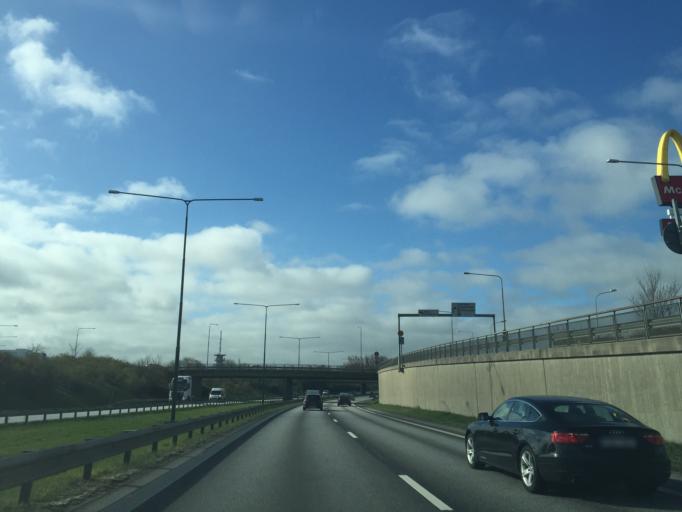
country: SE
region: Skane
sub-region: Burlovs Kommun
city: Arloev
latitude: 55.5841
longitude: 13.0562
